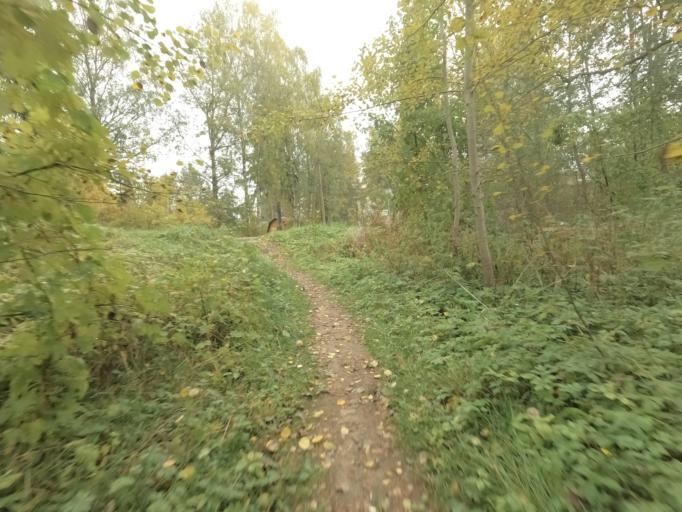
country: RU
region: Leningrad
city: Pavlovo
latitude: 59.7763
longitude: 30.9718
